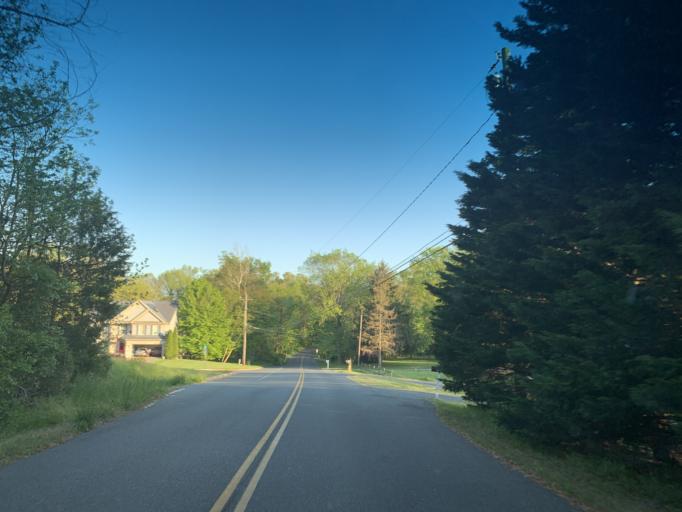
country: US
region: Maryland
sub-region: Harford County
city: Aberdeen
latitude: 39.5332
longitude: -76.1756
